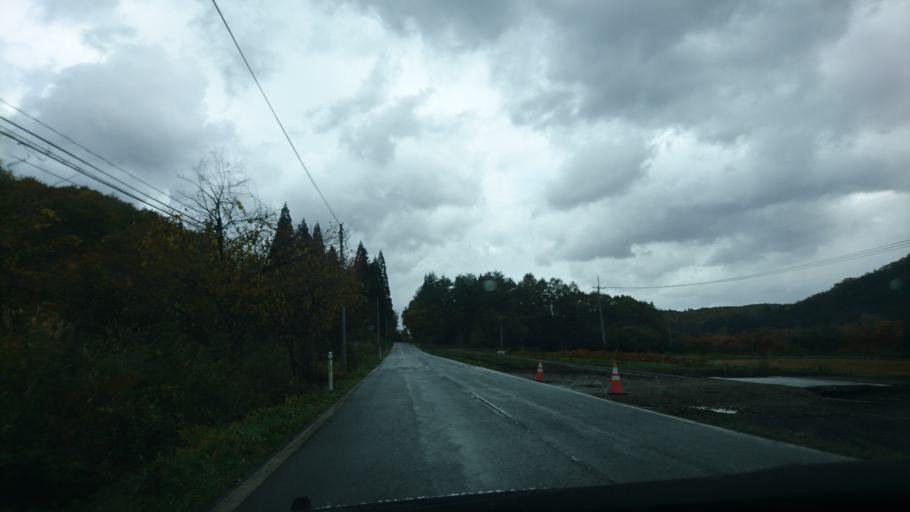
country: JP
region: Iwate
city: Shizukuishi
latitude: 39.6180
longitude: 140.9454
